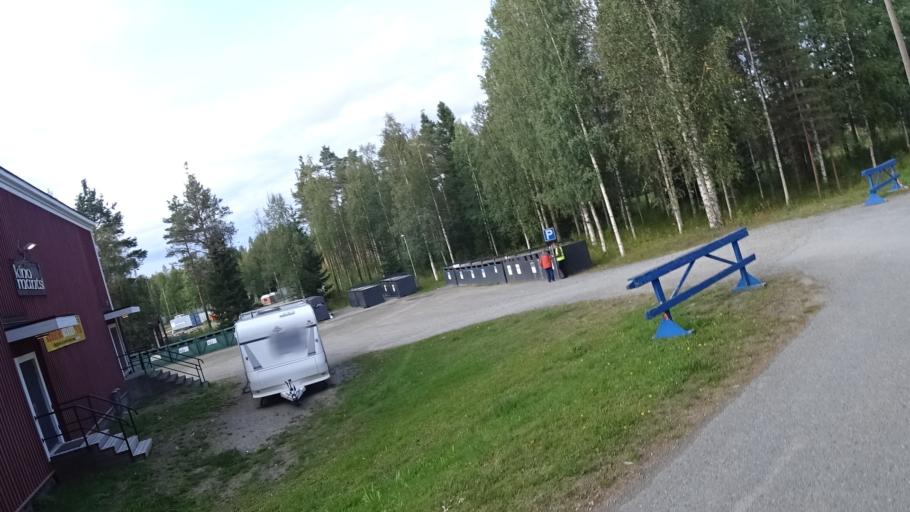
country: FI
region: North Karelia
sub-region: Joensuu
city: Ilomantsi
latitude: 62.6721
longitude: 30.9424
